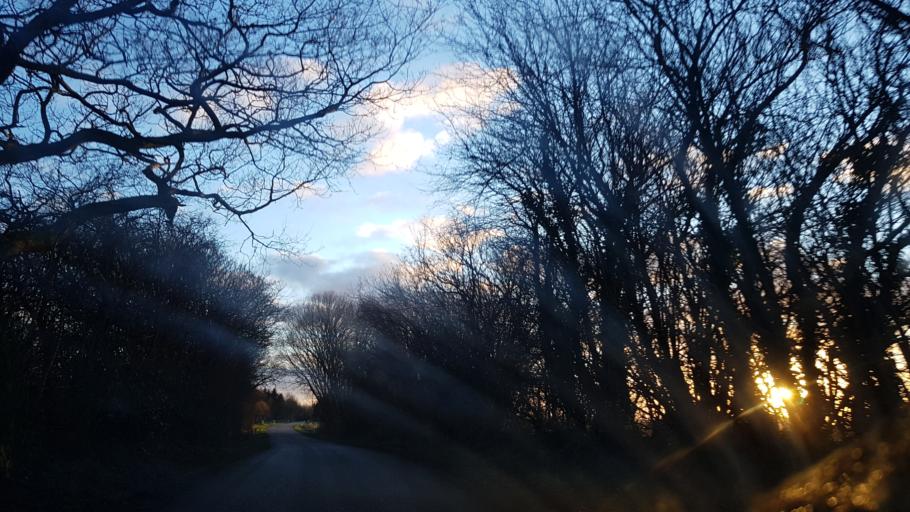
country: DK
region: South Denmark
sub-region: Kolding Kommune
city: Vamdrup
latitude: 55.3620
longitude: 9.2816
